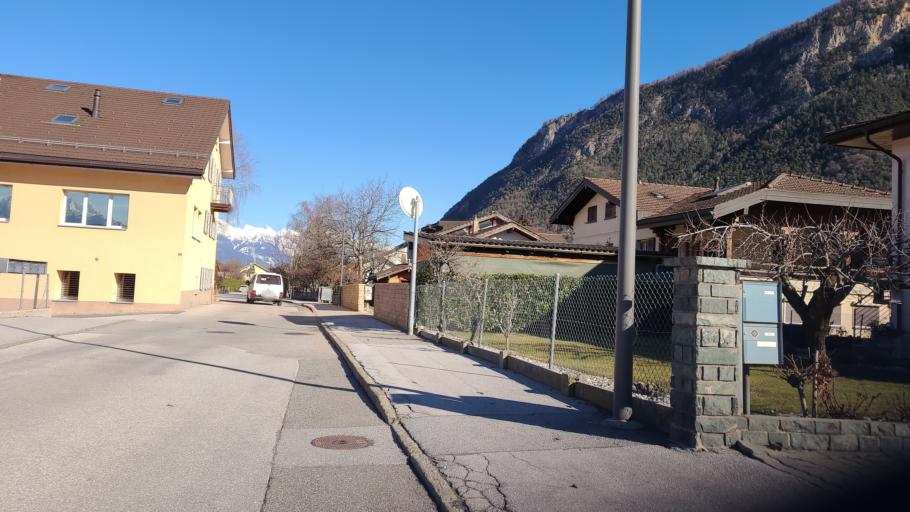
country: CH
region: Valais
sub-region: Herens District
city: Vex
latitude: 46.2335
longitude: 7.4000
